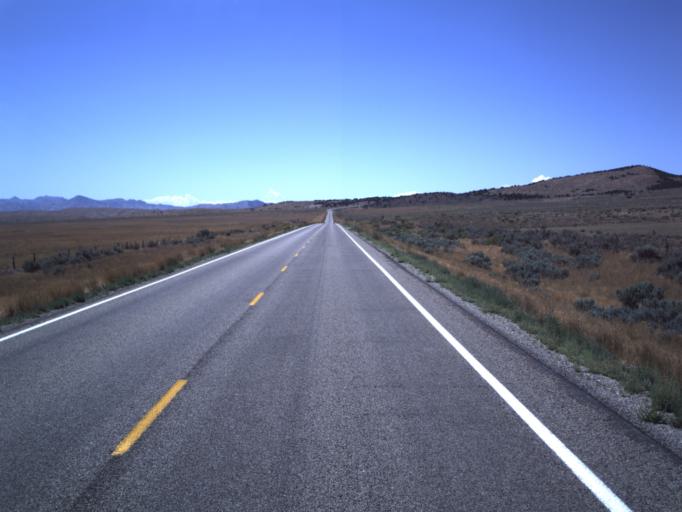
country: US
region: Utah
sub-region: Juab County
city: Nephi
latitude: 39.6810
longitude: -112.0144
